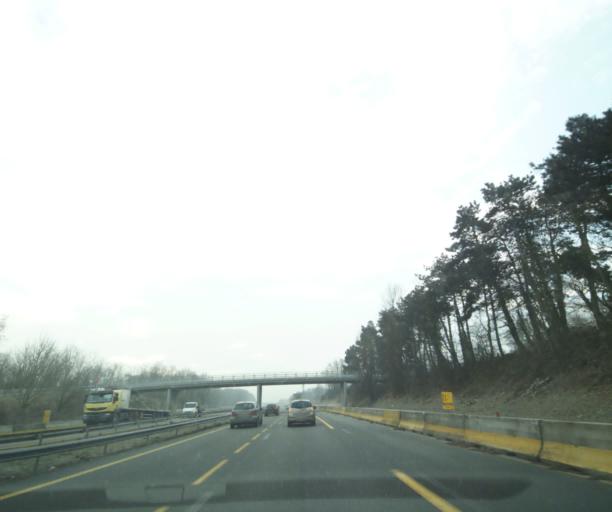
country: FR
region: Rhone-Alpes
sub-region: Departement du Rhone
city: Lissieu
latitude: 45.8459
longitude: 4.7479
